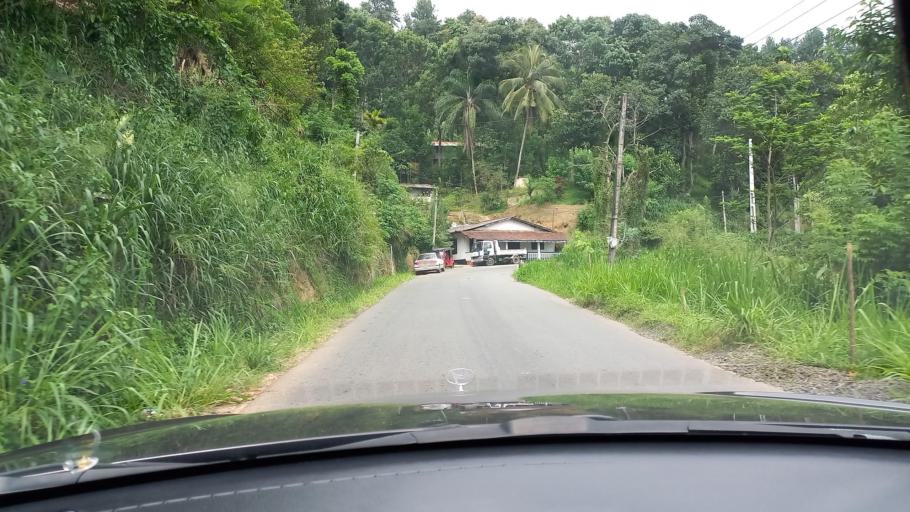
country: LK
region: Central
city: Gampola
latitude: 7.2103
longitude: 80.6203
